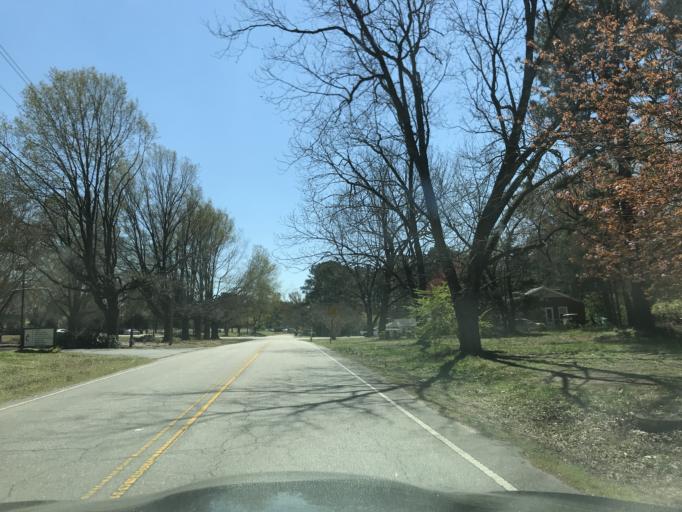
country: US
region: North Carolina
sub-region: Wake County
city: Raleigh
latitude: 35.8339
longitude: -78.5703
